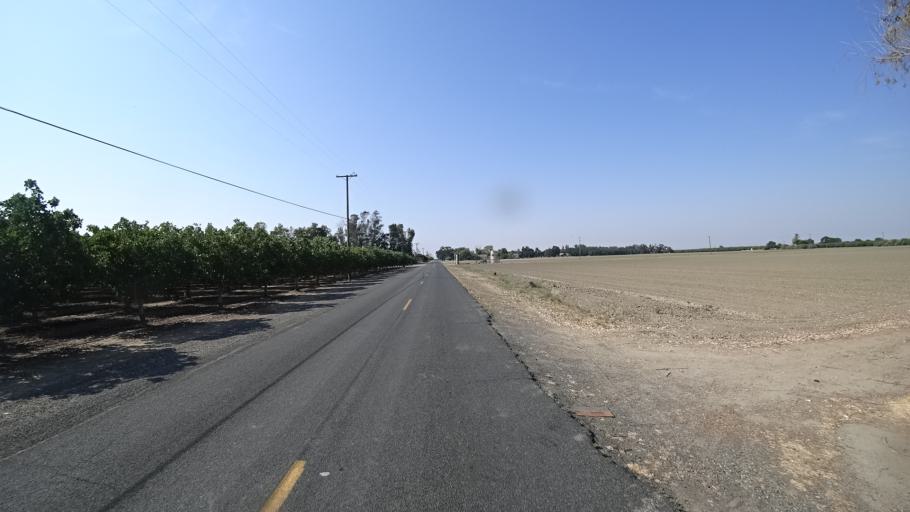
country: US
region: California
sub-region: Kings County
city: Lemoore
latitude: 36.3382
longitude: -119.8513
